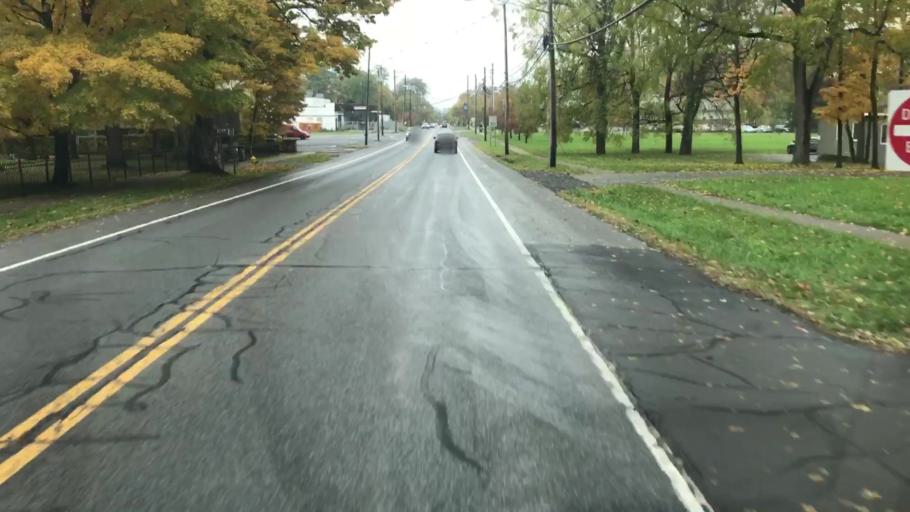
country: US
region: New York
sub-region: Onondaga County
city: Fayetteville
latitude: 43.0309
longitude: -75.9985
